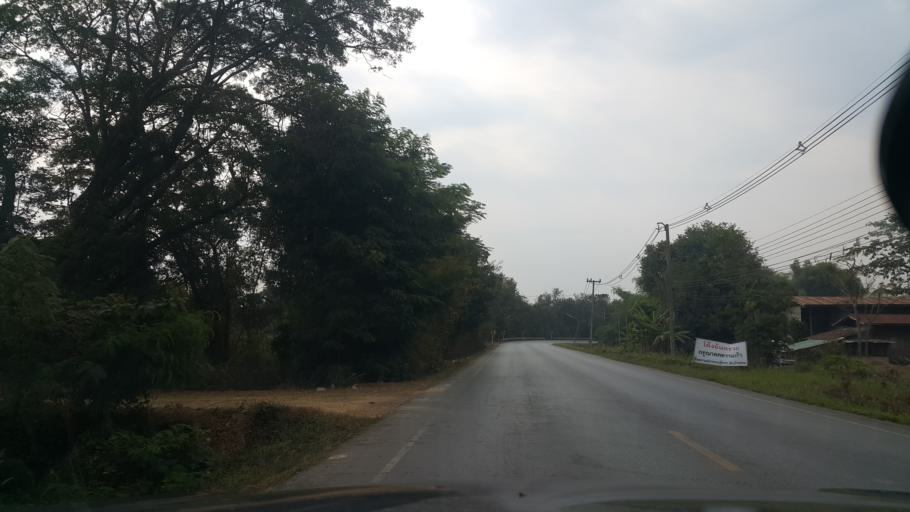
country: TH
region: Sukhothai
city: Sukhothai
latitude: 17.0708
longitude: 99.8802
